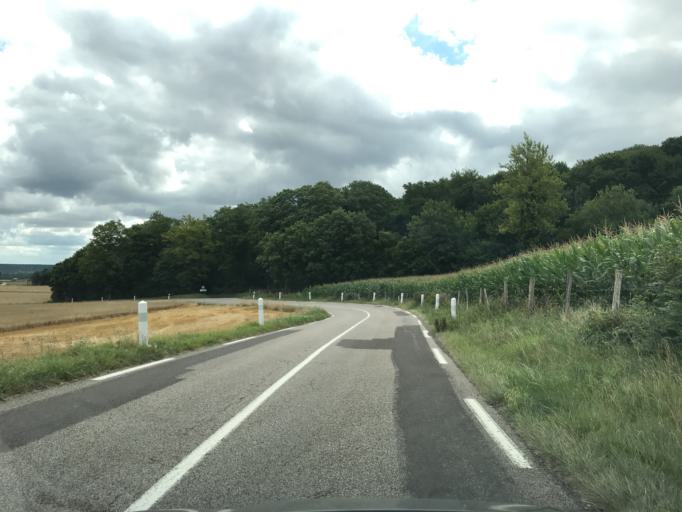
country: FR
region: Haute-Normandie
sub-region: Departement de l'Eure
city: Menilles
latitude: 49.0375
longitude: 1.2960
